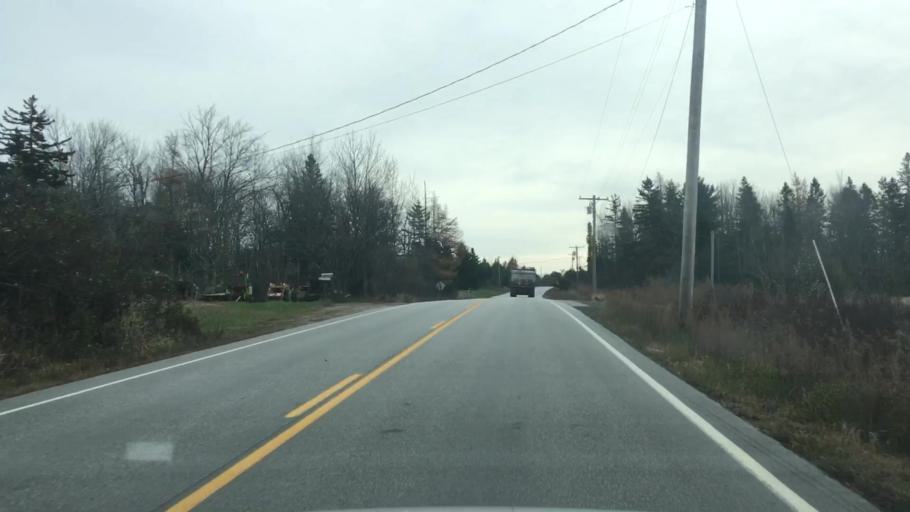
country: US
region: Maine
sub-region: Hancock County
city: Penobscot
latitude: 44.5285
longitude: -68.6696
